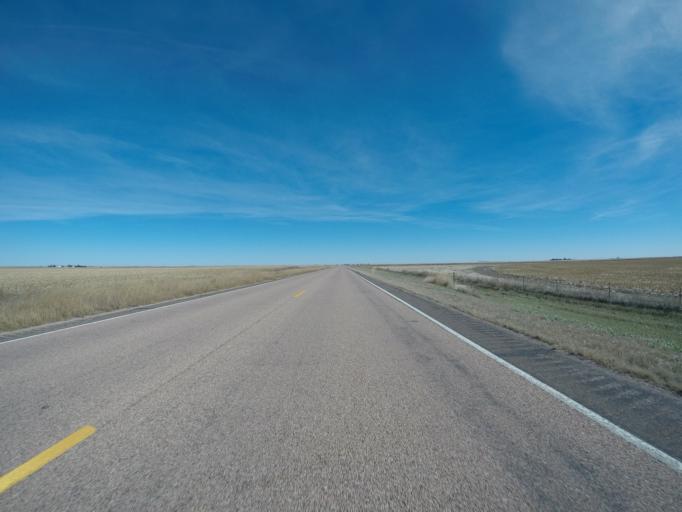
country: US
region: Colorado
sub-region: Yuma County
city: Yuma
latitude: 39.6562
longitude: -102.6062
